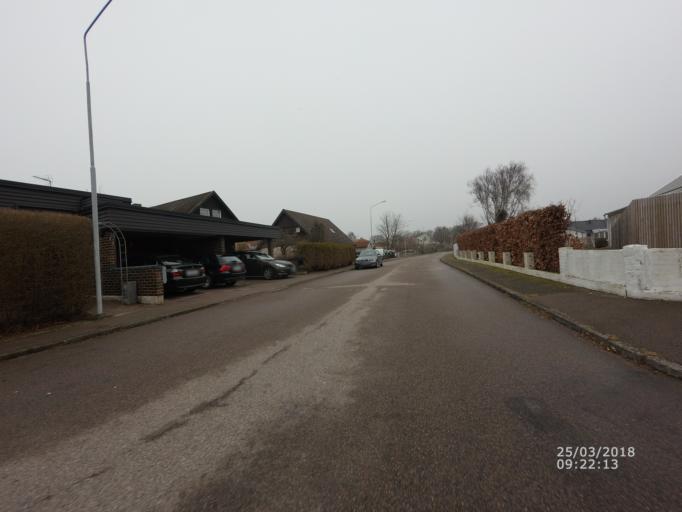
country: SE
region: Skane
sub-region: Hoganas Kommun
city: Hoganas
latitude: 56.1573
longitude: 12.5690
